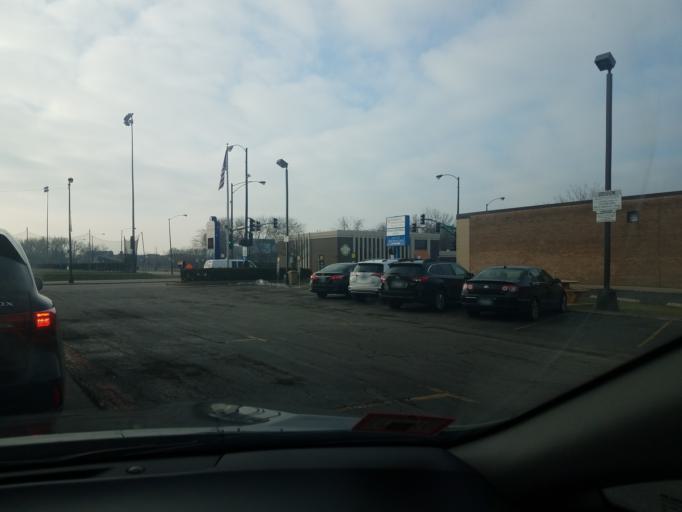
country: US
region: Illinois
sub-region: Cook County
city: Lincolnwood
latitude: 41.9471
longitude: -87.6938
